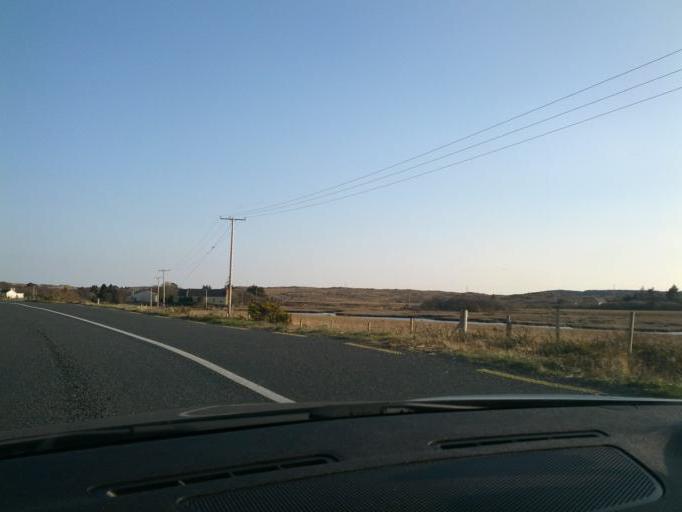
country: IE
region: Connaught
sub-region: County Galway
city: Oughterard
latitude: 53.3793
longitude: -9.5490
